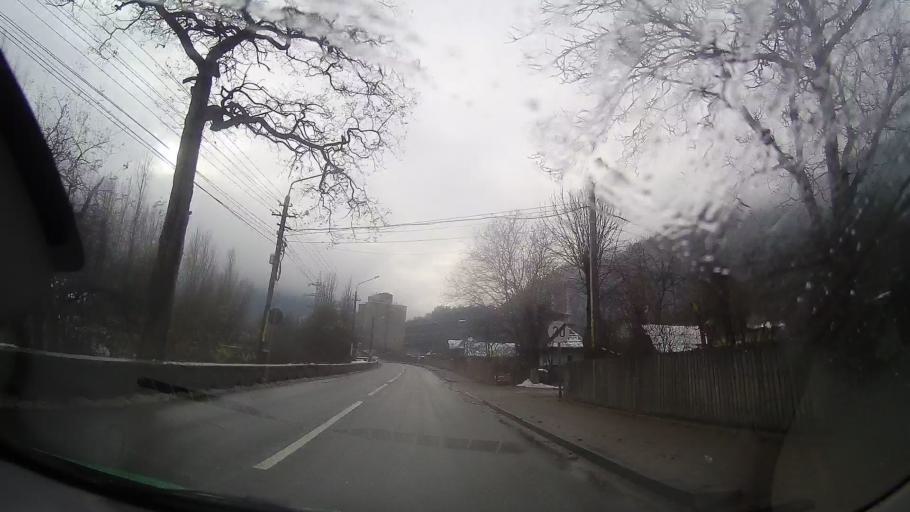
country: RO
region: Neamt
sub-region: Comuna Bicaz
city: Bicaz
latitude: 46.9071
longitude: 26.0783
